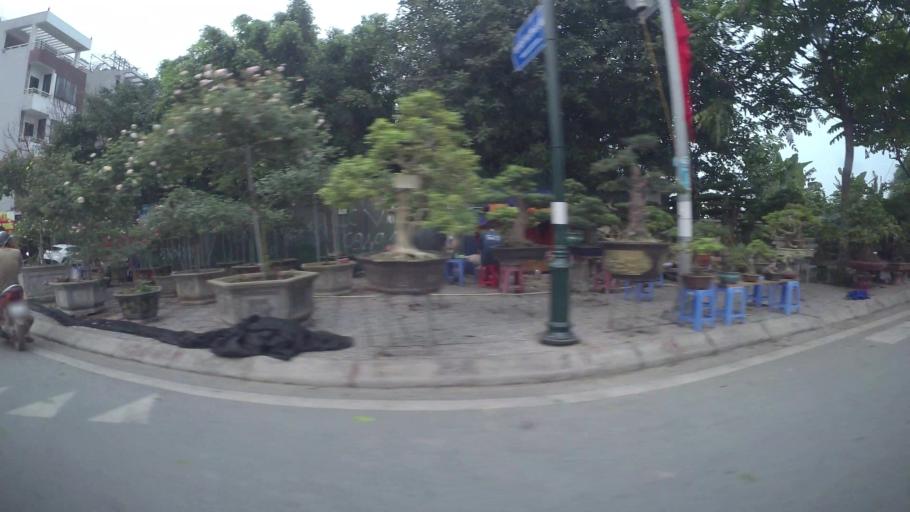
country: VN
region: Ha Noi
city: Hoan Kiem
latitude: 21.0545
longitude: 105.8925
